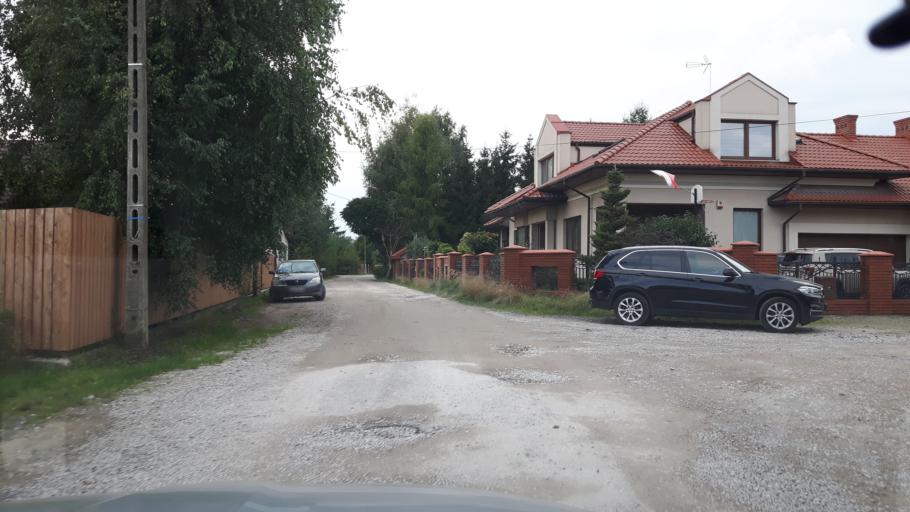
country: PL
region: Masovian Voivodeship
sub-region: Warszawa
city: Targowek
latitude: 52.3150
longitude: 21.0495
